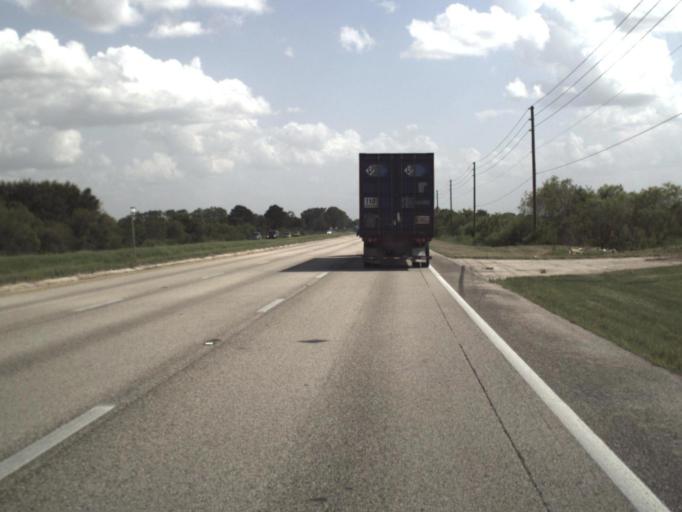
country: US
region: Florida
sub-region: Polk County
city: Lake Wales
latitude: 27.9468
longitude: -81.6167
